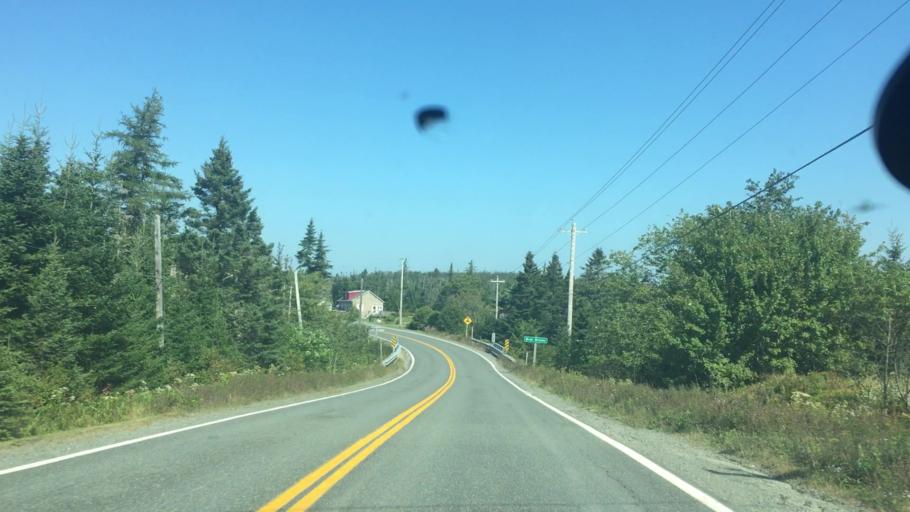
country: CA
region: Nova Scotia
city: Antigonish
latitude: 44.9990
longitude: -62.0997
